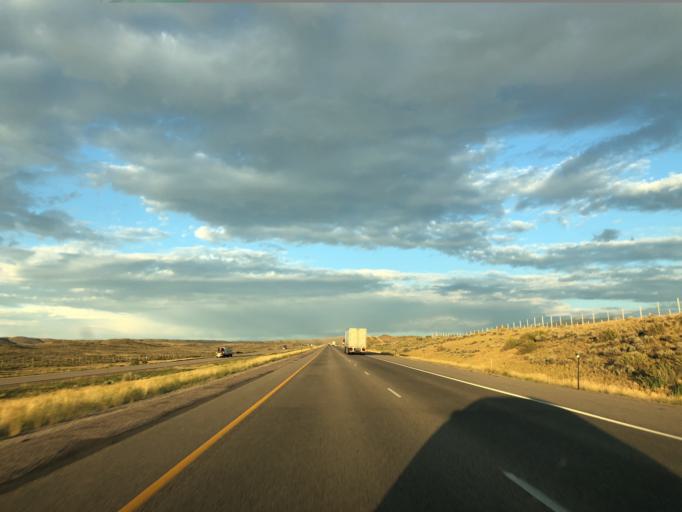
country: US
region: Wyoming
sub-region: Carbon County
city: Saratoga
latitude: 41.7329
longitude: -106.7213
